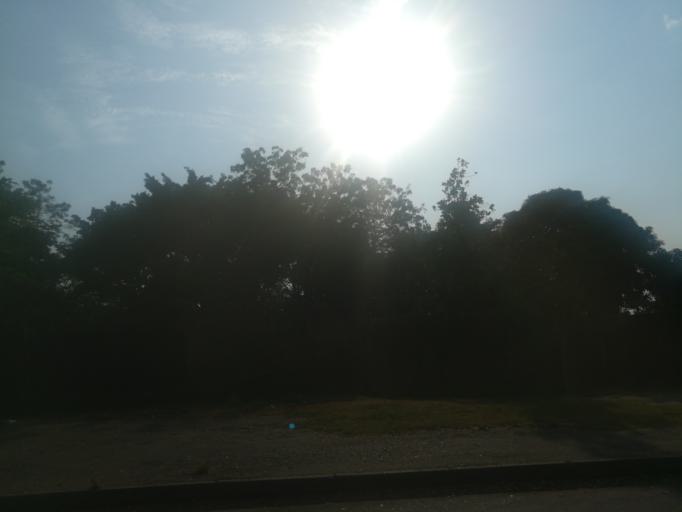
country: NG
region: Abuja Federal Capital Territory
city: Abuja
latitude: 9.0638
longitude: 7.4517
